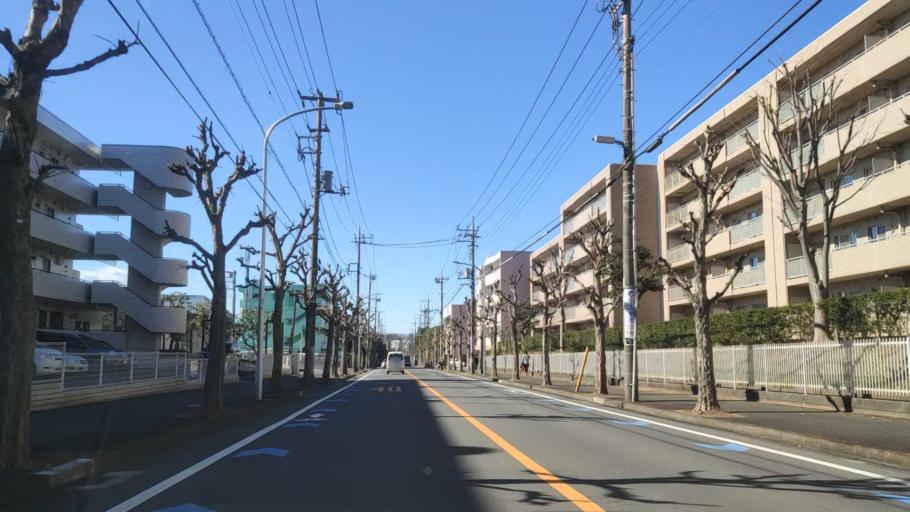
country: JP
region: Tokyo
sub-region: Machida-shi
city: Machida
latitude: 35.5540
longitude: 139.5025
